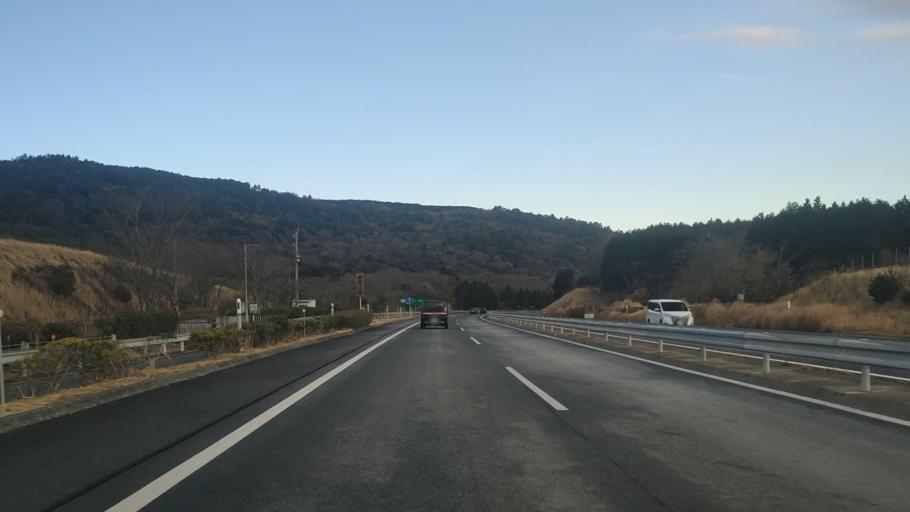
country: JP
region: Oita
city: Beppu
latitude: 33.3405
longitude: 131.4261
